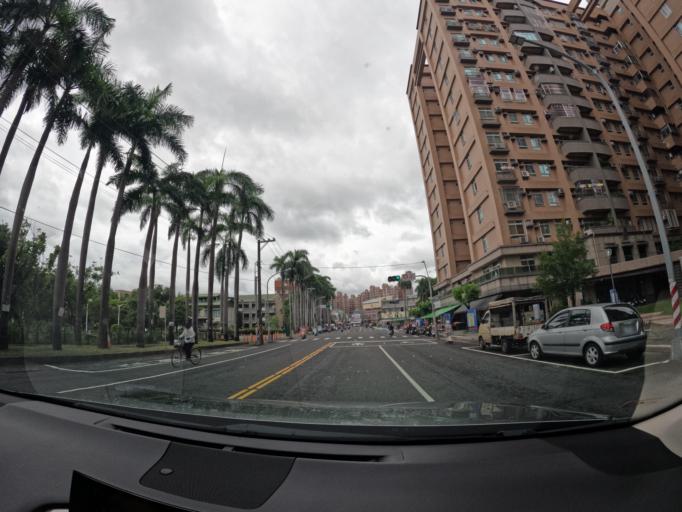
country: TW
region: Taiwan
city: Fengshan
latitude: 22.6285
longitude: 120.3738
